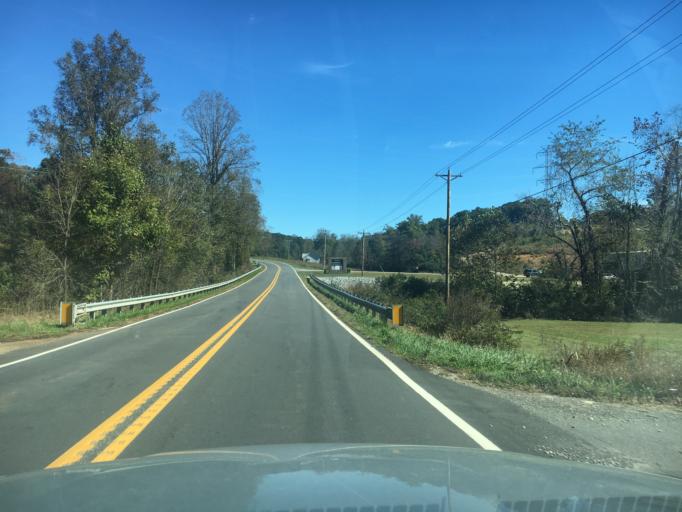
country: US
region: North Carolina
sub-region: Burke County
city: Salem
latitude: 35.6645
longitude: -81.7456
